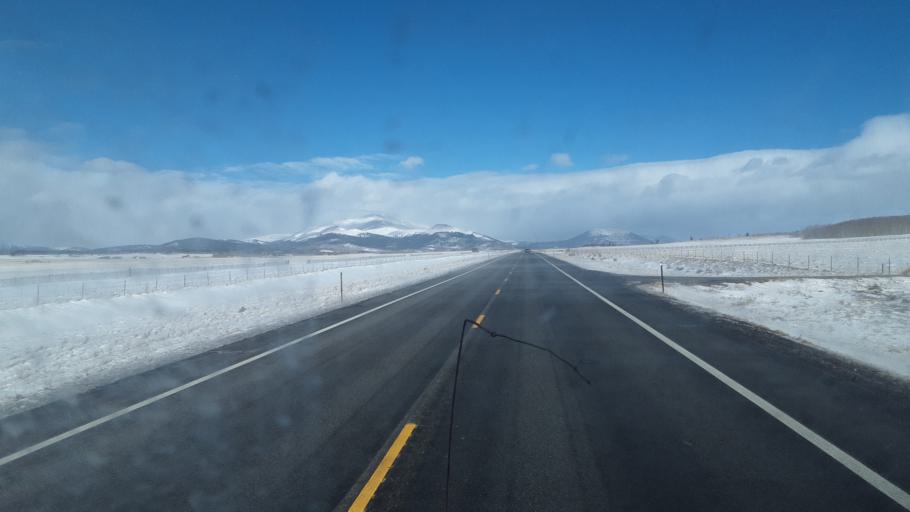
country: US
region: Colorado
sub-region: Park County
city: Fairplay
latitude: 39.1835
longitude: -105.9990
